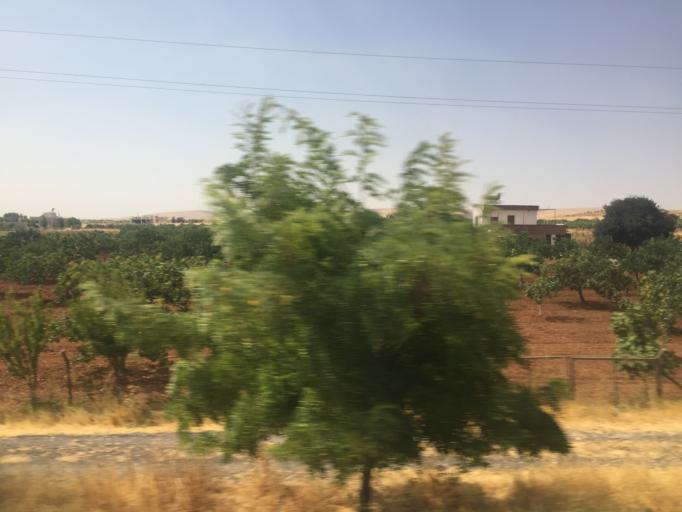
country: TR
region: Sanliurfa
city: Akziyaret
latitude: 37.3885
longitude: 38.8577
